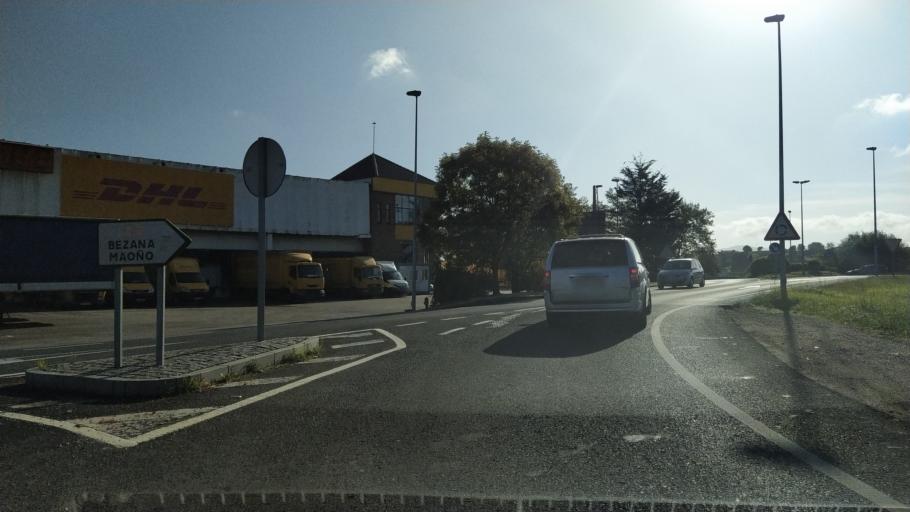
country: ES
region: Cantabria
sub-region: Provincia de Cantabria
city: Santa Cruz de Bezana
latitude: 43.4314
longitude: -3.9177
